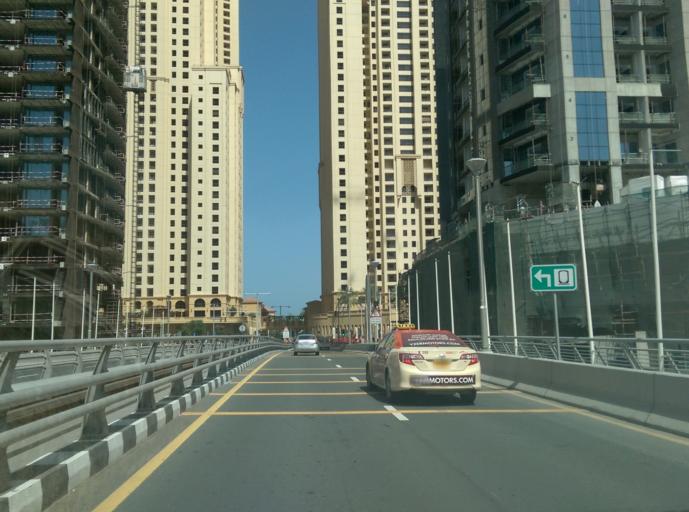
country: AE
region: Dubai
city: Dubai
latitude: 25.0799
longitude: 55.1408
